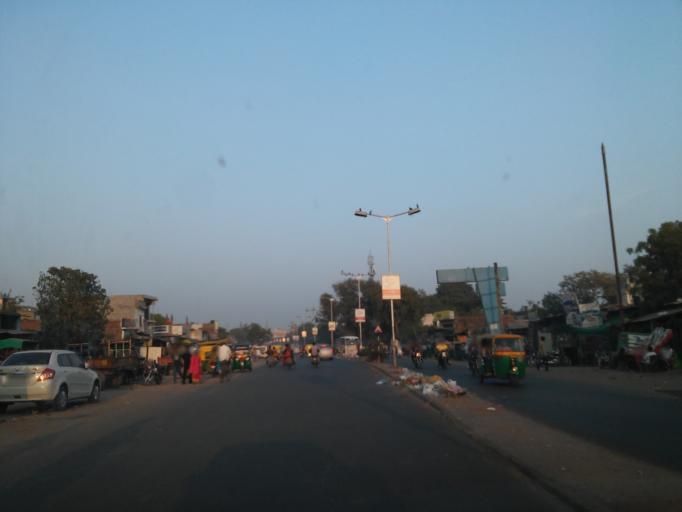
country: IN
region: Gujarat
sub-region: Ahmadabad
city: Sarkhej
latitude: 22.9968
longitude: 72.5385
